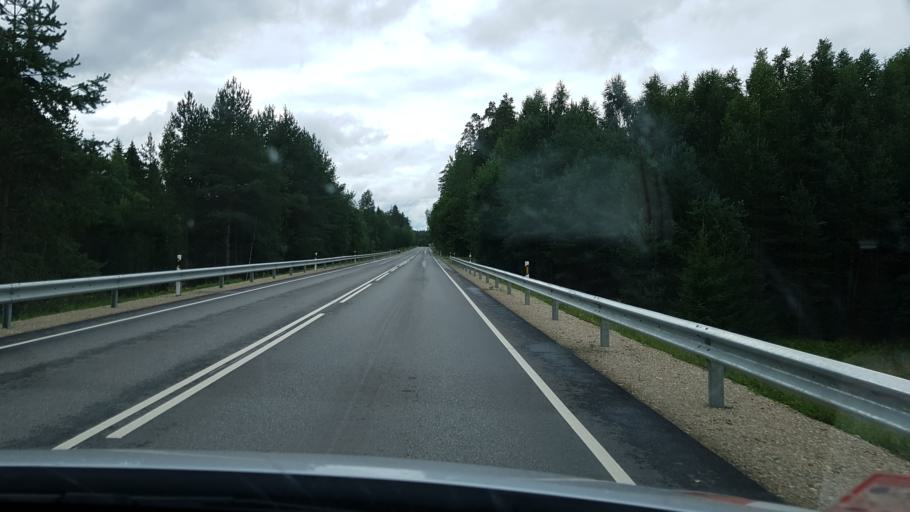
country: EE
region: Polvamaa
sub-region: Polva linn
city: Polva
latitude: 58.0208
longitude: 27.1649
